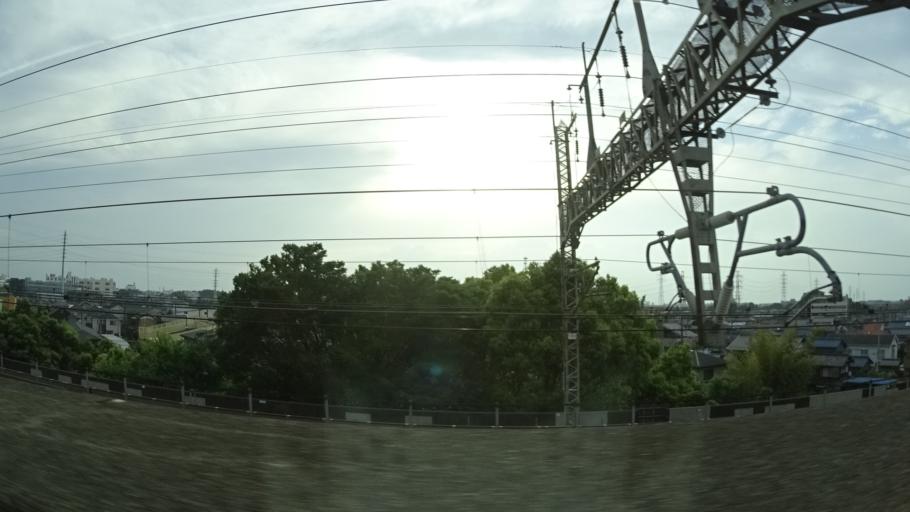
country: JP
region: Saitama
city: Ageoshimo
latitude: 35.9675
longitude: 139.6230
